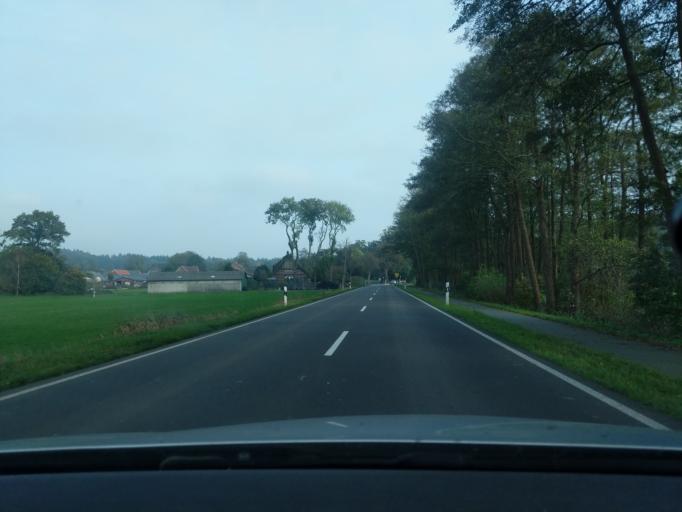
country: DE
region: Lower Saxony
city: Kranenburg
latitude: 53.6235
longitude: 9.1793
